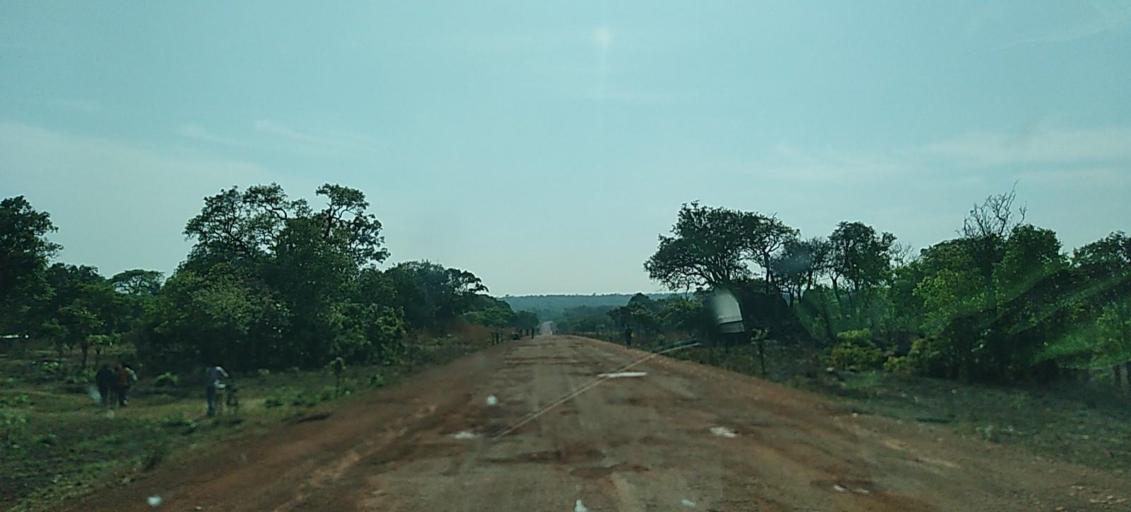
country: ZM
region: North-Western
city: Mwinilunga
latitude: -11.7861
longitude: 25.0326
